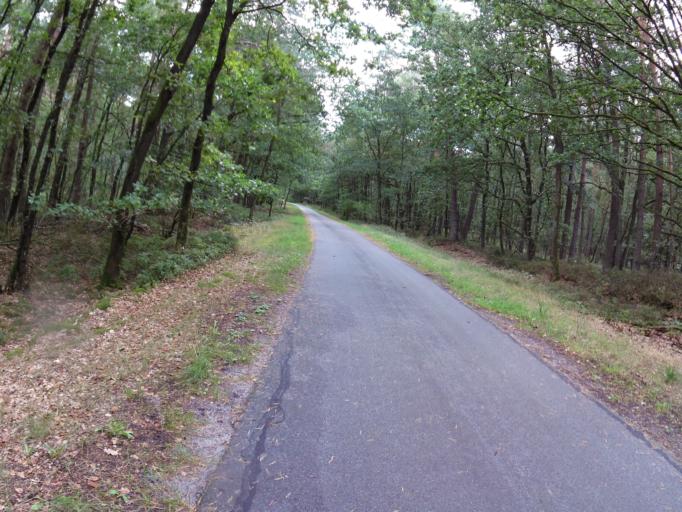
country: DE
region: Lower Saxony
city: Selsingen
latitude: 53.3629
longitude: 9.1690
